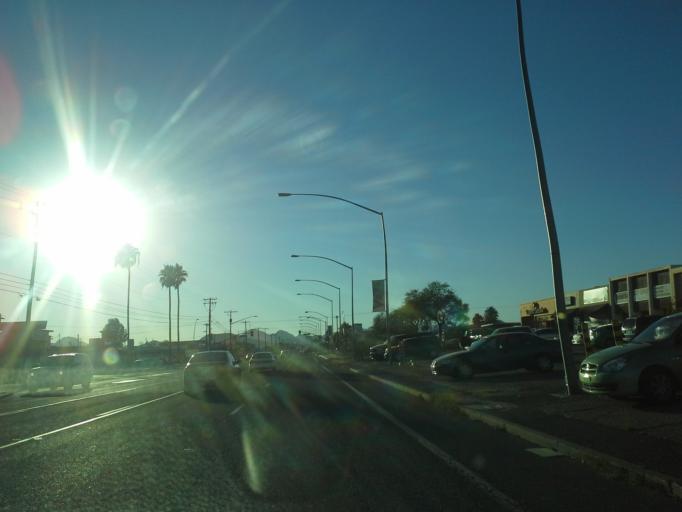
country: US
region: Arizona
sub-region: Pima County
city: Tucson
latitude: 32.2216
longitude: -110.9332
